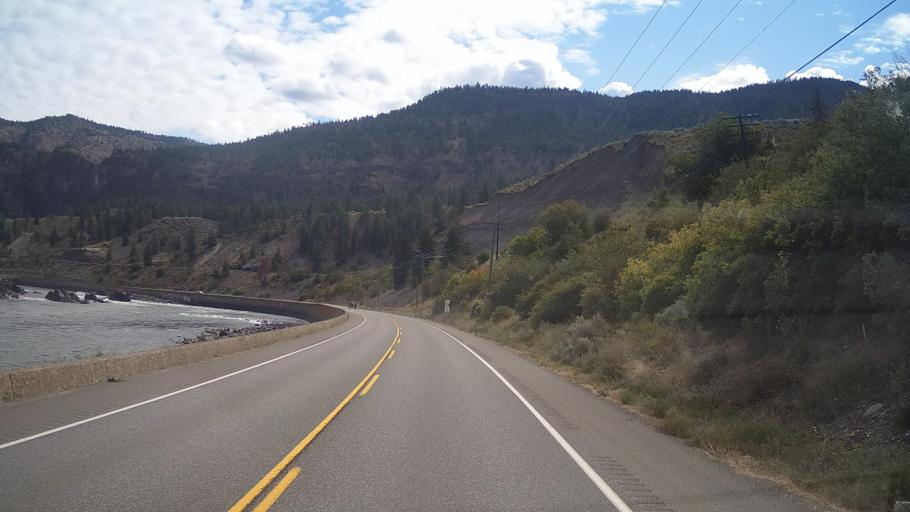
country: CA
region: British Columbia
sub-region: Thompson-Nicola Regional District
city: Ashcroft
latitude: 50.2629
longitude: -121.4123
